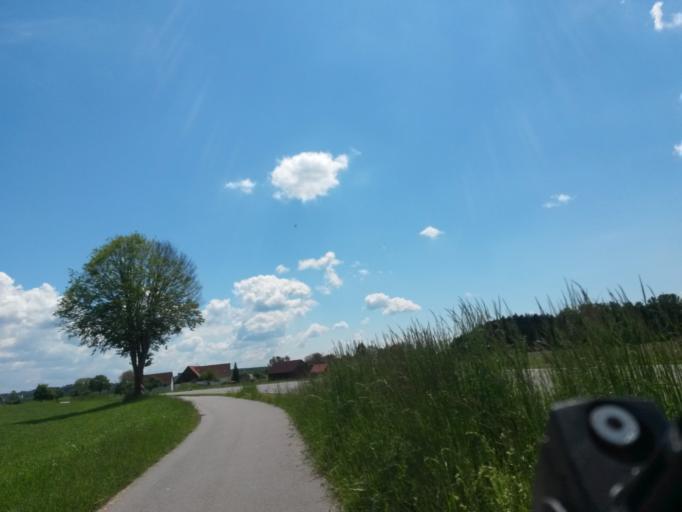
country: DE
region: Baden-Wuerttemberg
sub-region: Tuebingen Region
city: Bad Waldsee
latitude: 47.9441
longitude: 9.7454
